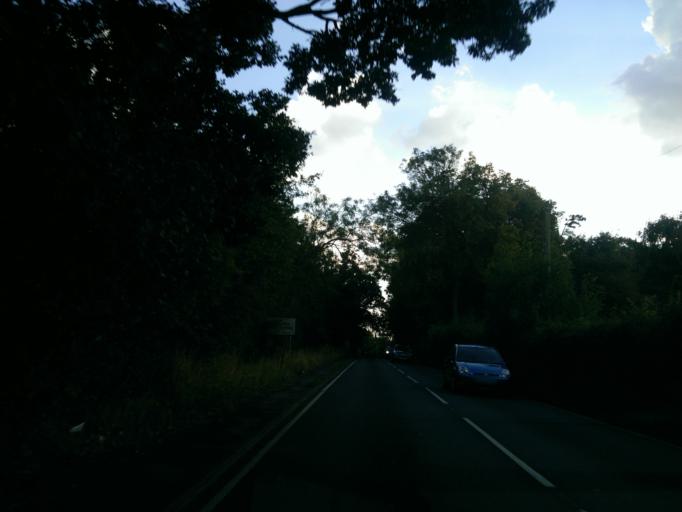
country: GB
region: England
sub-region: Essex
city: Braintree
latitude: 51.9179
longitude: 0.5841
